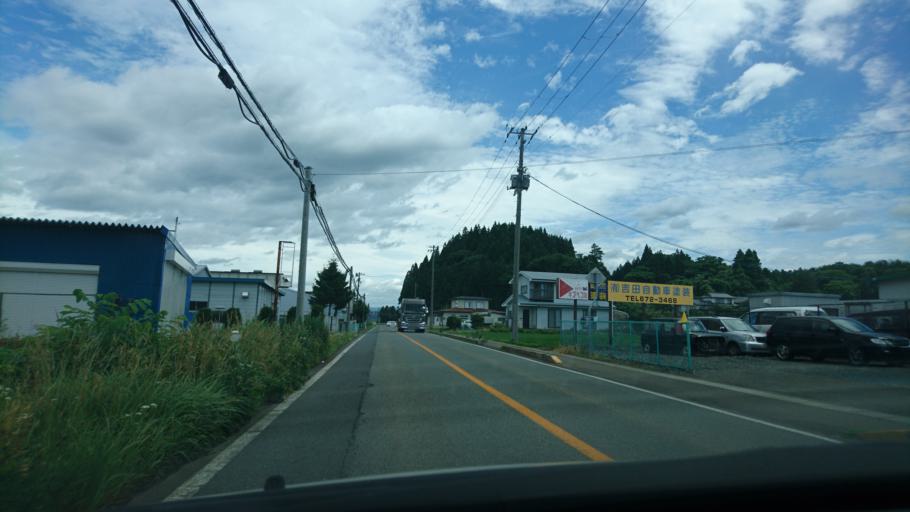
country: JP
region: Iwate
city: Morioka-shi
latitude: 39.5627
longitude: 141.1788
